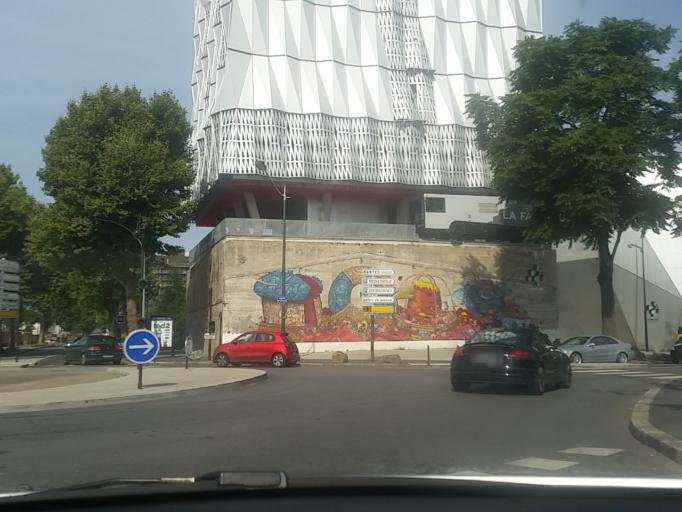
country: FR
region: Pays de la Loire
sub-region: Departement de la Loire-Atlantique
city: Nantes
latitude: 47.2046
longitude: -1.5622
